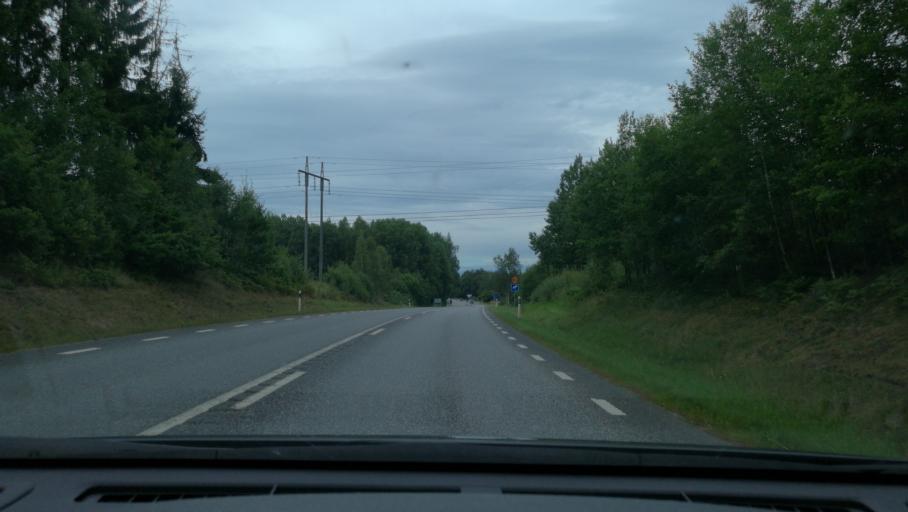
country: SE
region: Soedermanland
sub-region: Katrineholms Kommun
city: Katrineholm
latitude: 58.9639
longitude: 16.1916
